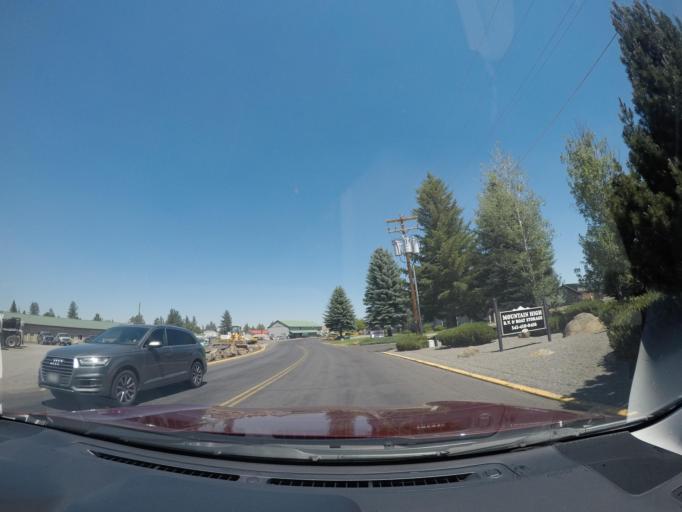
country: US
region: Oregon
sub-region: Deschutes County
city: Sisters
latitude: 44.2972
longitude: -121.5525
